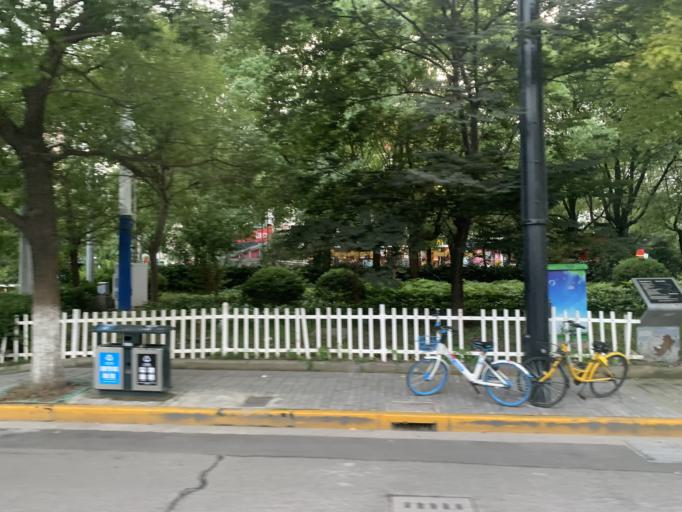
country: CN
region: Shanghai Shi
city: Huamu
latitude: 31.2083
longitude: 121.5265
